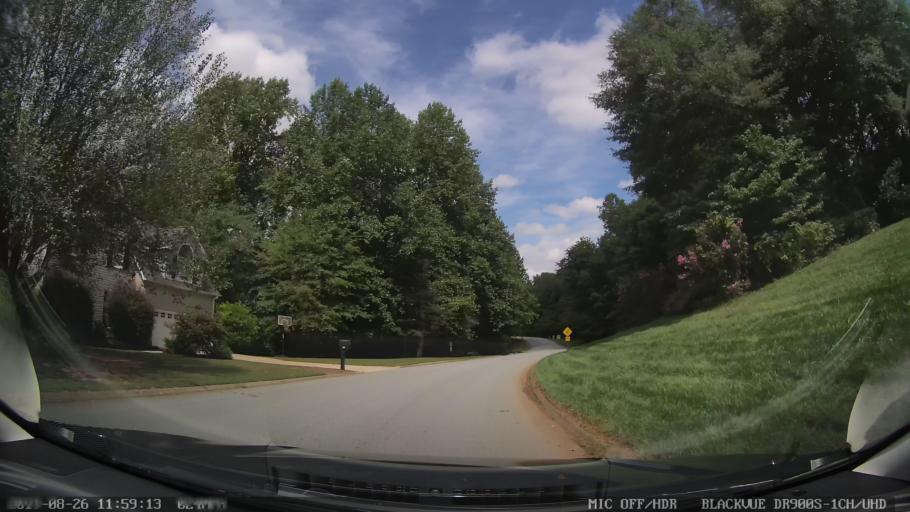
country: US
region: South Carolina
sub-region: Greenville County
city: Five Forks
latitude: 34.7948
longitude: -82.2322
